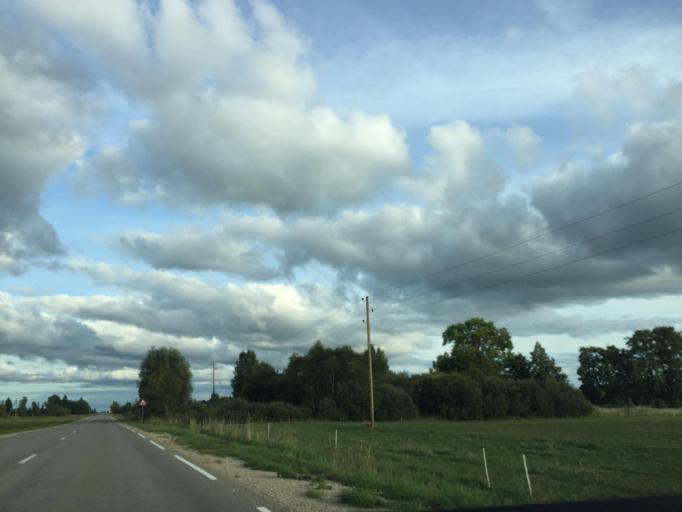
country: LV
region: Nereta
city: Nereta
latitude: 56.2568
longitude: 25.2023
